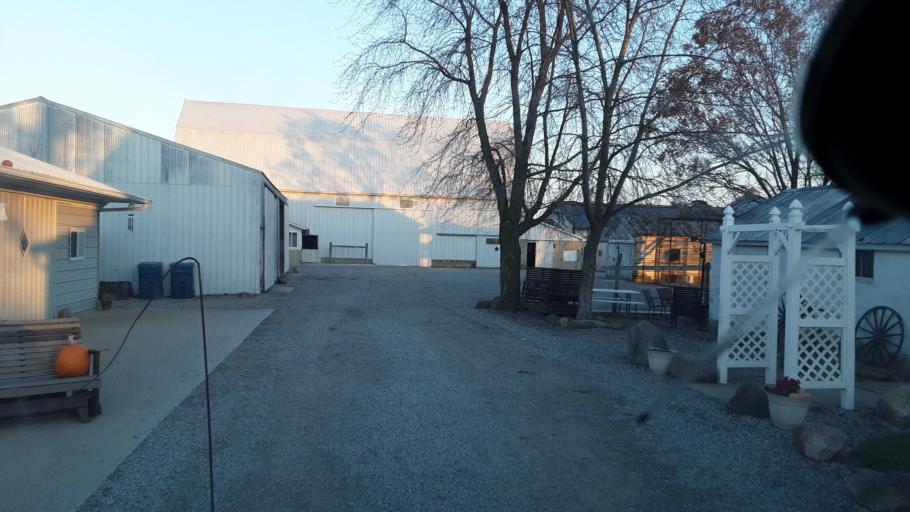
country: US
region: Indiana
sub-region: Allen County
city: Grabill
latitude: 41.2194
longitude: -84.9417
